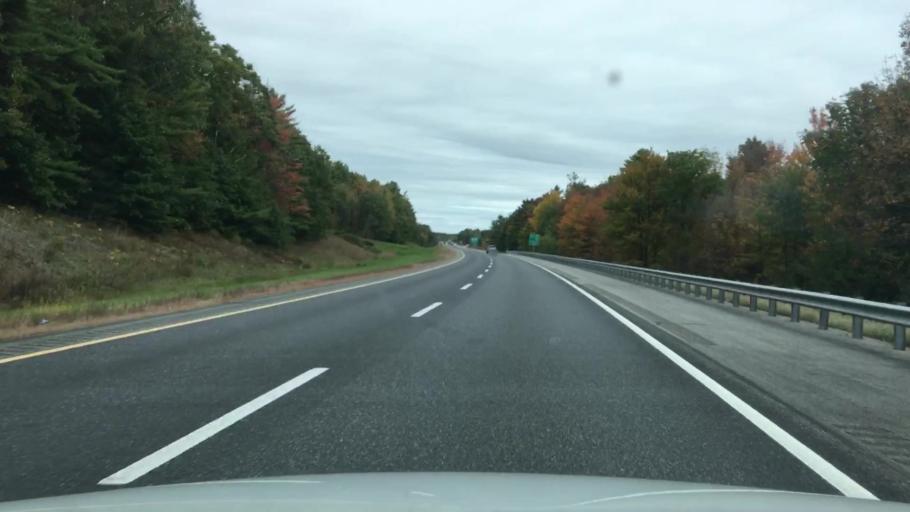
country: US
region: Maine
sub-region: Sagadahoc County
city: Topsham
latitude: 44.0082
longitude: -69.9225
